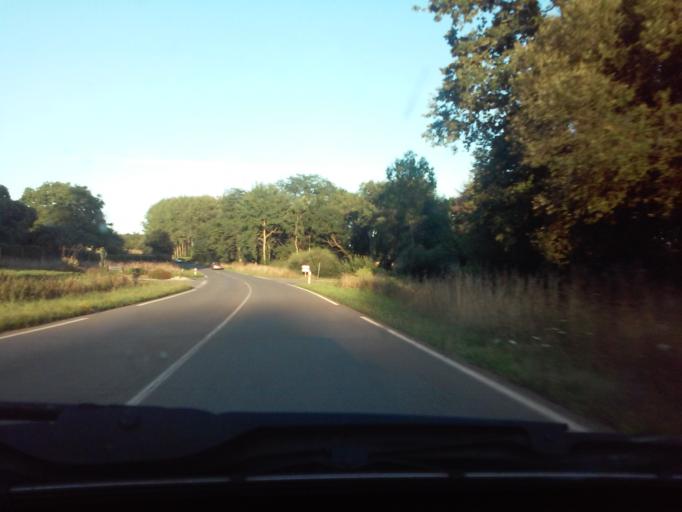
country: FR
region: Brittany
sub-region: Departement des Cotes-d'Armor
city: Les Champs-Geraux
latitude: 48.4446
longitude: -1.9883
